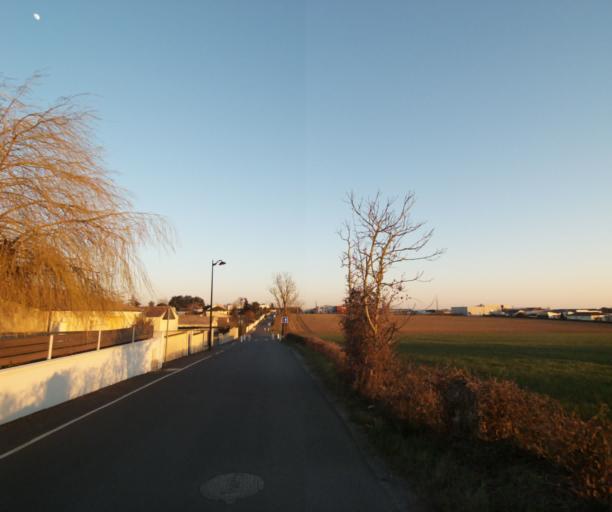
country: FR
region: Poitou-Charentes
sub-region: Departement des Deux-Sevres
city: Niort
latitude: 46.3410
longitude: -0.4236
